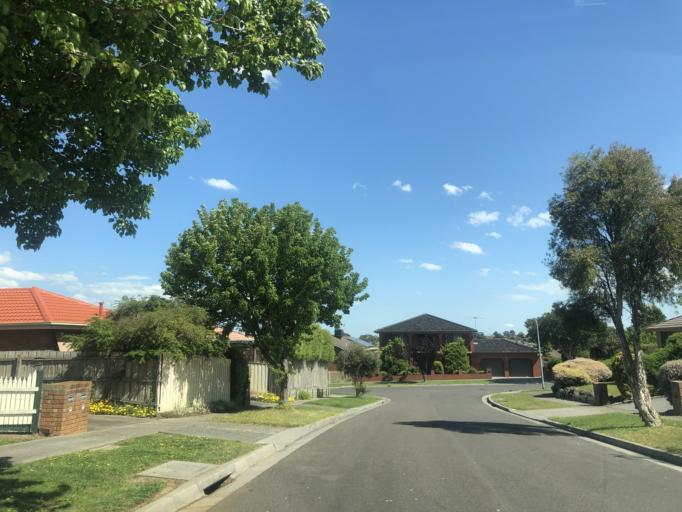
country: AU
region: Victoria
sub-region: Casey
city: Endeavour Hills
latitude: -37.9919
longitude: 145.2634
